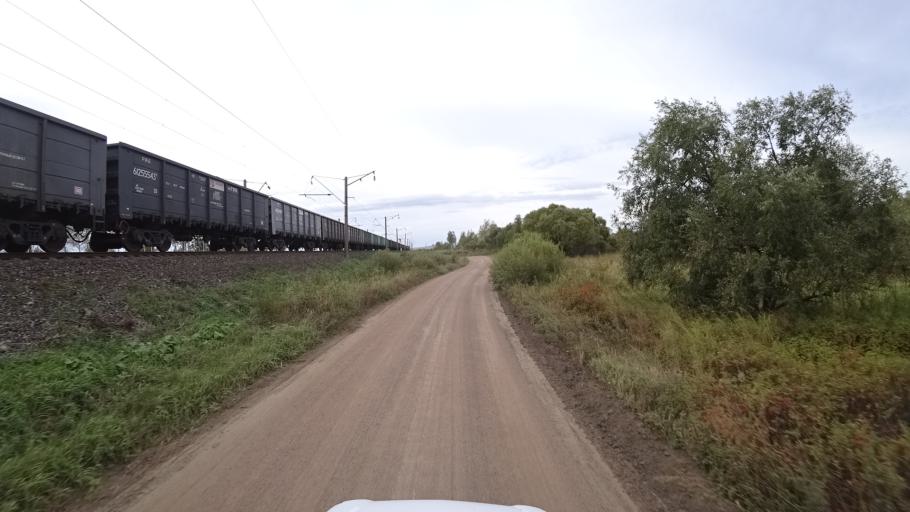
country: RU
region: Amur
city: Arkhara
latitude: 49.3650
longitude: 130.1456
